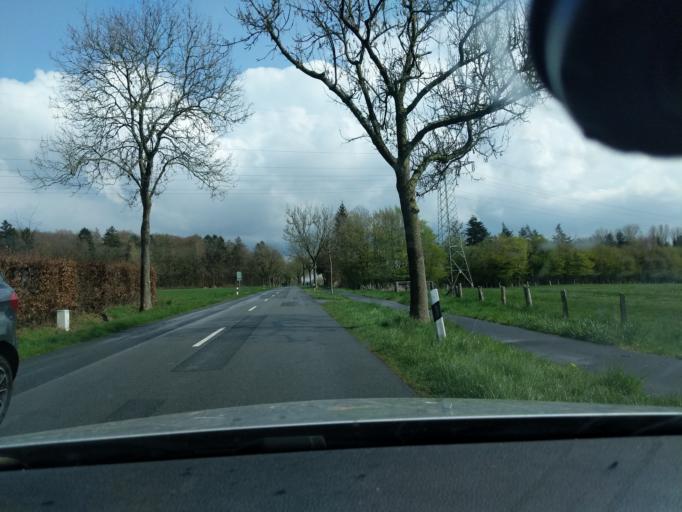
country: DE
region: Lower Saxony
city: Harsefeld
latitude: 53.4626
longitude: 9.4884
